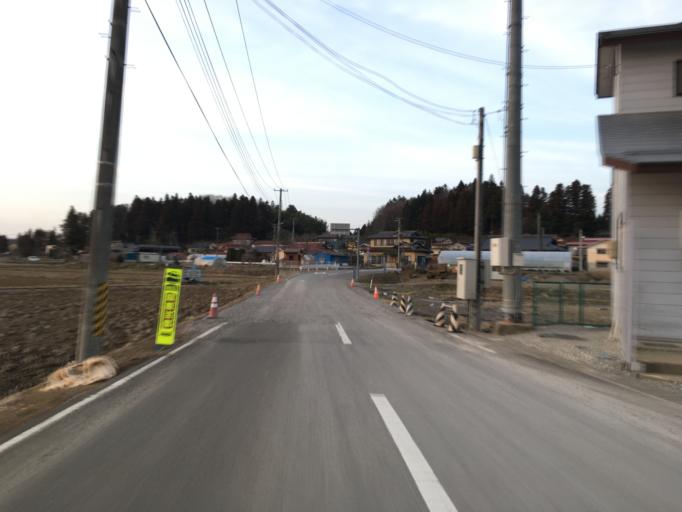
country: JP
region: Fukushima
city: Ishikawa
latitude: 37.0641
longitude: 140.3483
